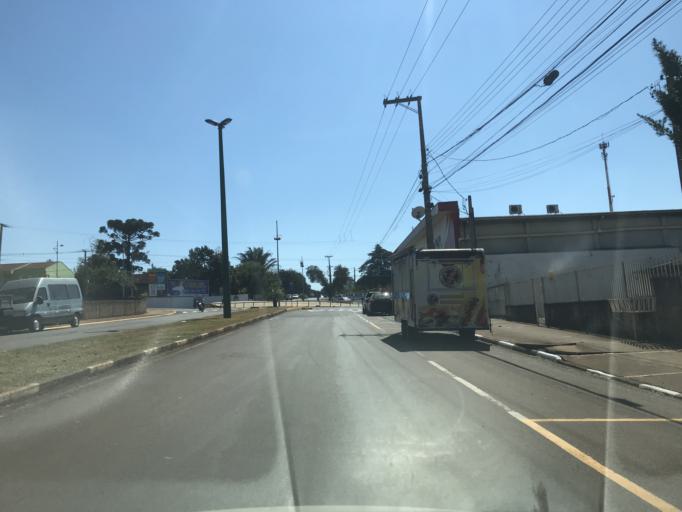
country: BR
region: Parana
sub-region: Toledo
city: Toledo
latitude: -24.7276
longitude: -53.7360
